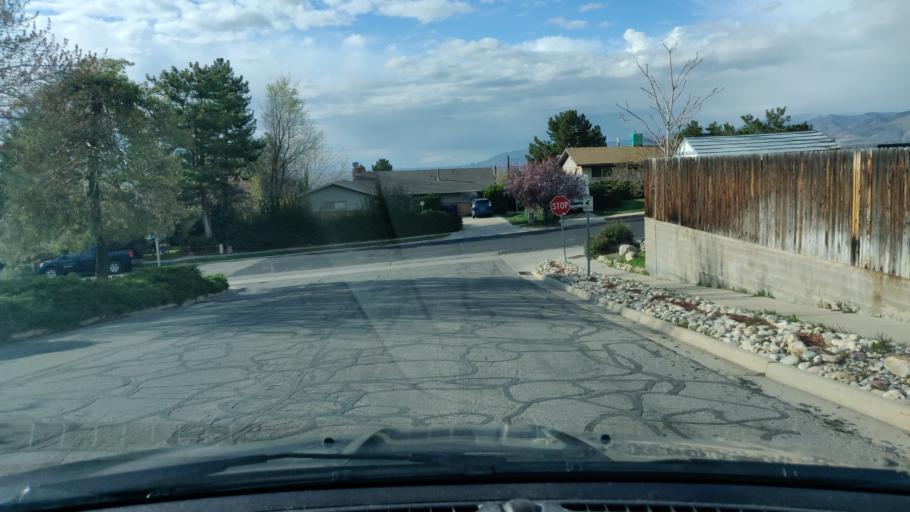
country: US
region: Utah
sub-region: Salt Lake County
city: Cottonwood Heights
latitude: 40.6201
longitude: -111.8206
